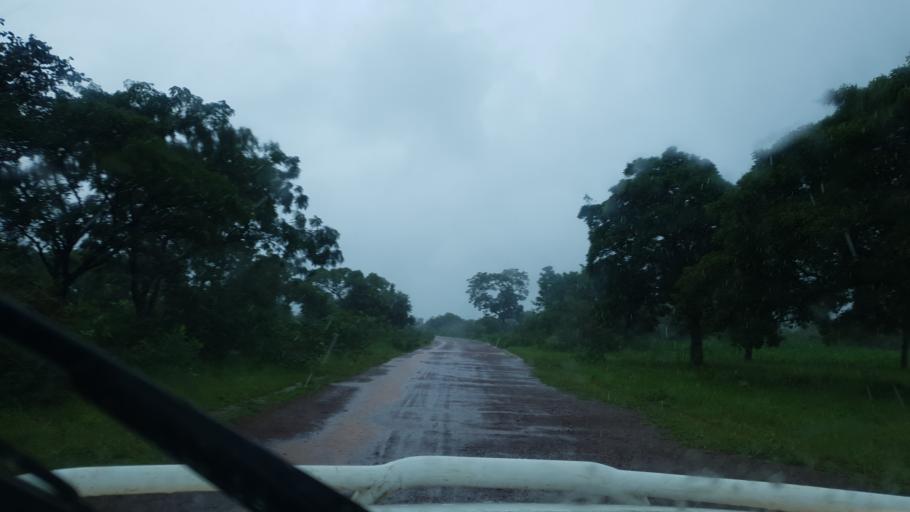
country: ML
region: Sikasso
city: Kolondieba
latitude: 11.6081
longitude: -6.6752
